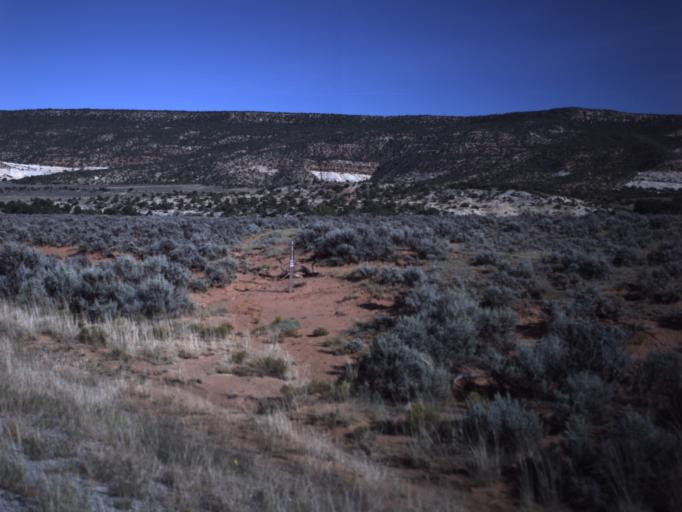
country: US
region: Utah
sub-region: San Juan County
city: Monticello
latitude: 38.0056
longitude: -109.4492
